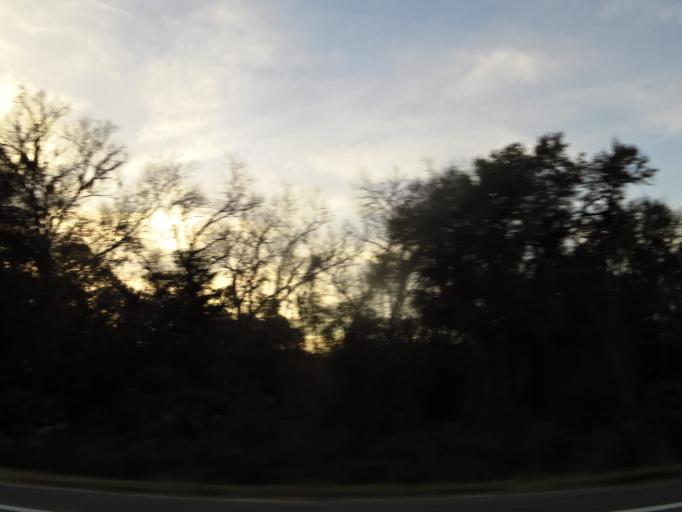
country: US
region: Florida
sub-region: Volusia County
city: De Leon Springs
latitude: 29.1095
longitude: -81.2939
